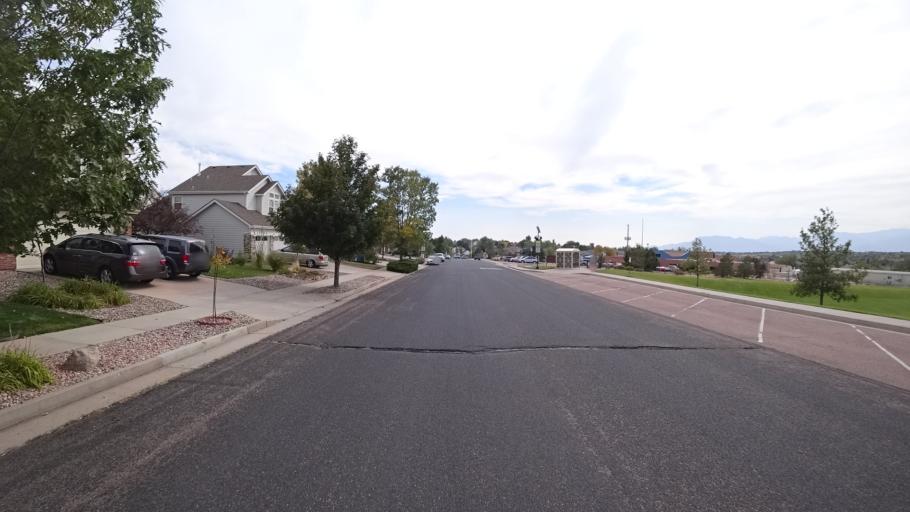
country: US
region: Colorado
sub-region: El Paso County
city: Cimarron Hills
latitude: 38.9073
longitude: -104.6997
